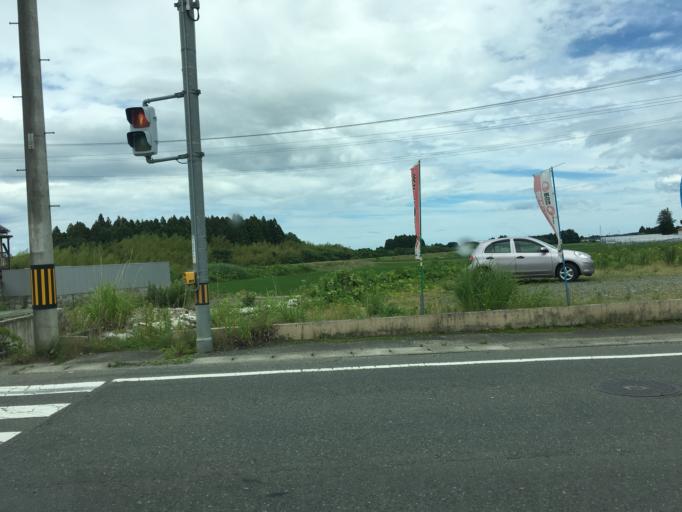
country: JP
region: Fukushima
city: Namie
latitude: 37.7229
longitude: 140.9302
